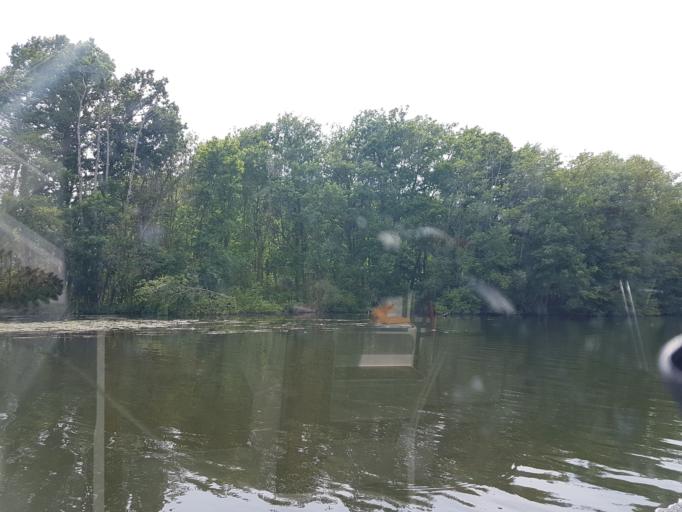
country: FR
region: Bourgogne
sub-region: Departement de l'Yonne
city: Gurgy
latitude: 47.8599
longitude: 3.5540
